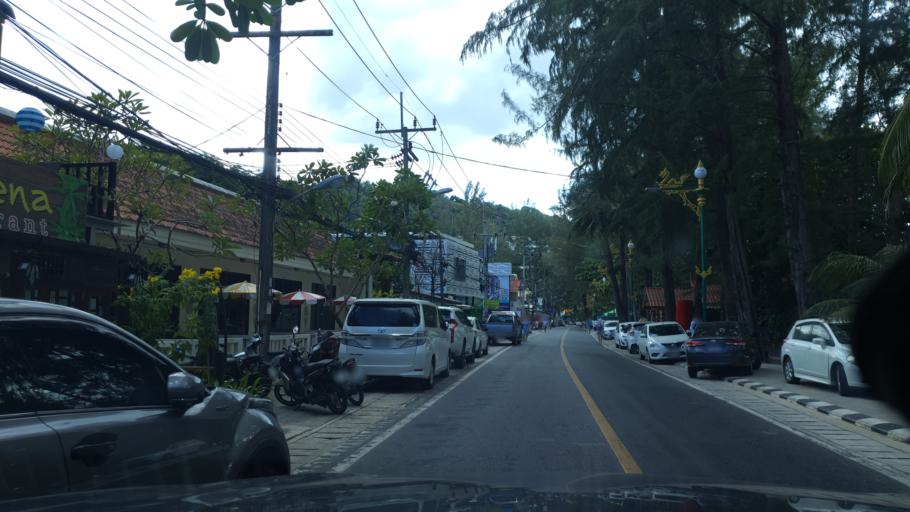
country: TH
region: Phuket
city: Thalang
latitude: 8.0592
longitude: 98.2780
